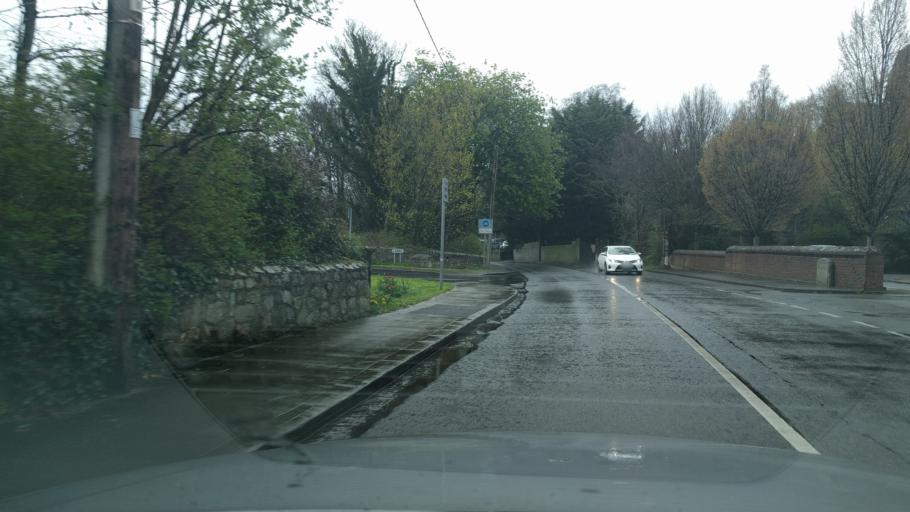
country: IE
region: Leinster
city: Ballyboden
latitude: 53.2776
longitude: -6.2969
